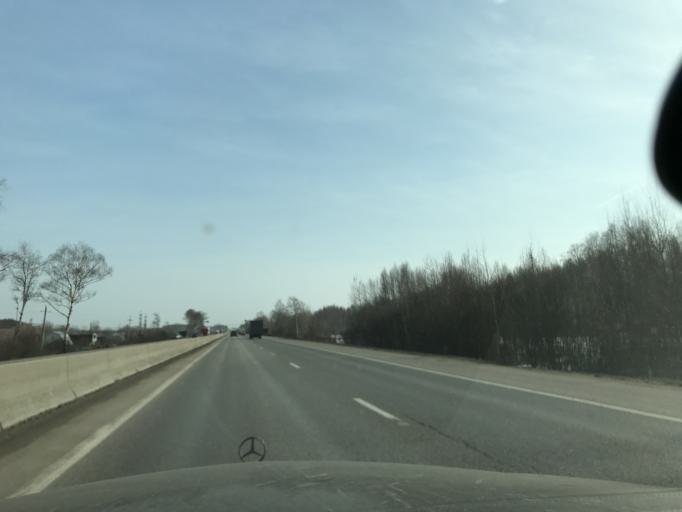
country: RU
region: Nizjnij Novgorod
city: Babino
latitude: 56.3051
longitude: 43.6464
